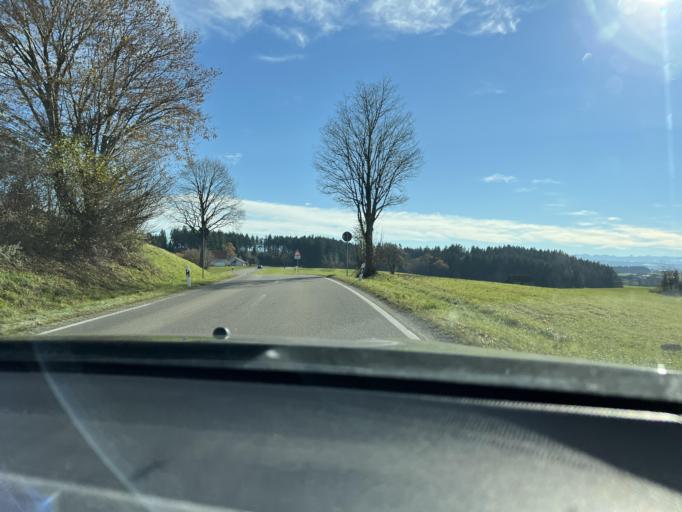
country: DE
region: Bavaria
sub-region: Swabia
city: Gestratz
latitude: 47.7202
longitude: 9.9639
